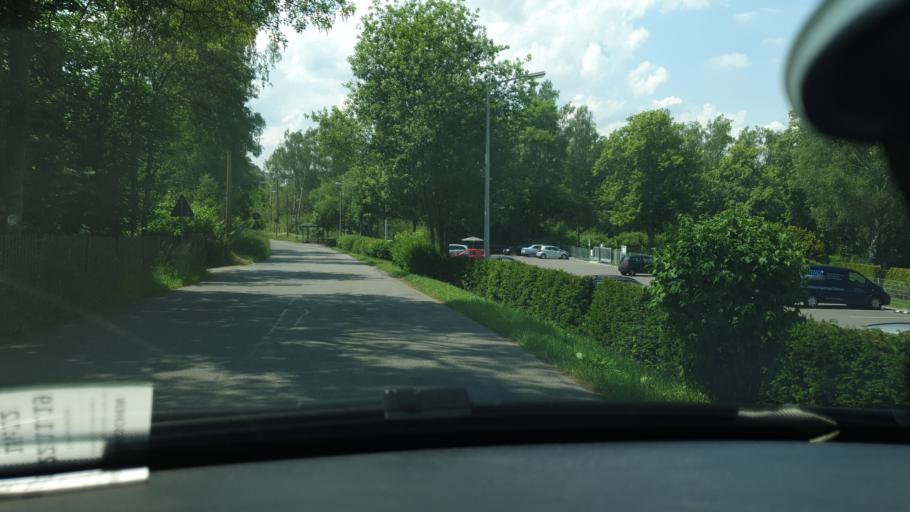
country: DE
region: Saxony
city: Freiberg
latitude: 50.9213
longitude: 13.3597
